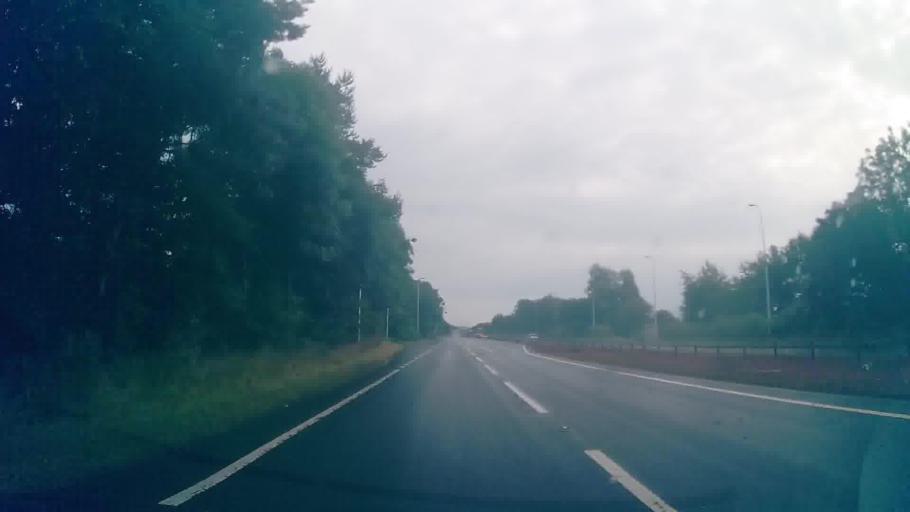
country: GB
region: Scotland
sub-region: Dumfries and Galloway
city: Locharbriggs
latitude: 55.0668
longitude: -3.5235
